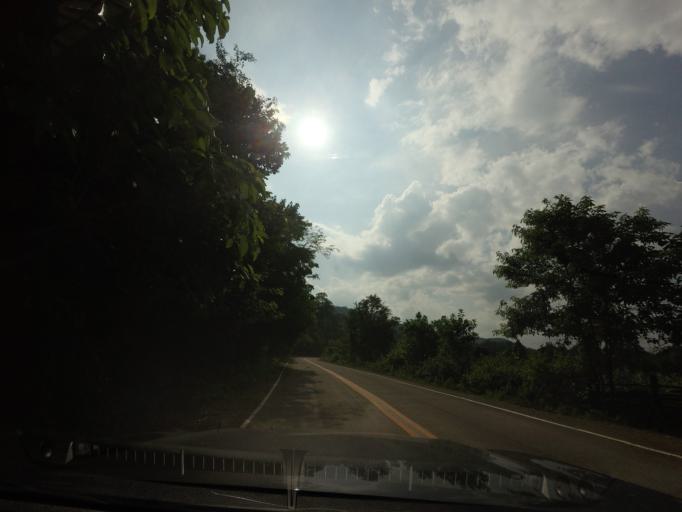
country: TH
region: Nan
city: Na Noi
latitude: 18.2816
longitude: 100.9444
